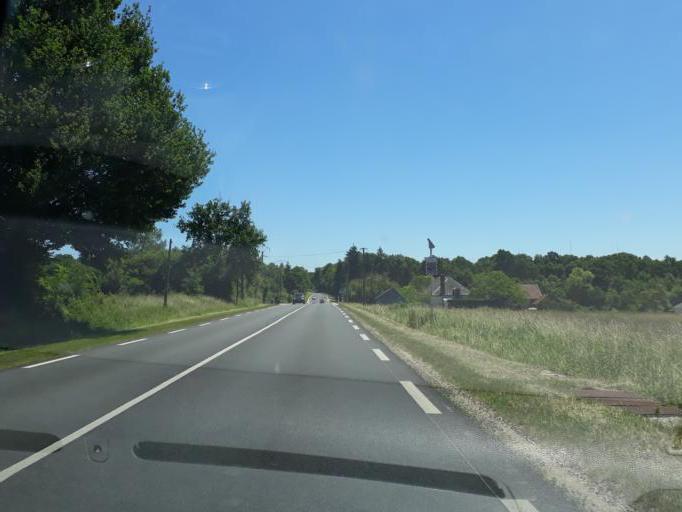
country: FR
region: Centre
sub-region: Departement du Cher
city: Vignoux-sur-Barangeon
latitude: 47.2084
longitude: 2.1481
